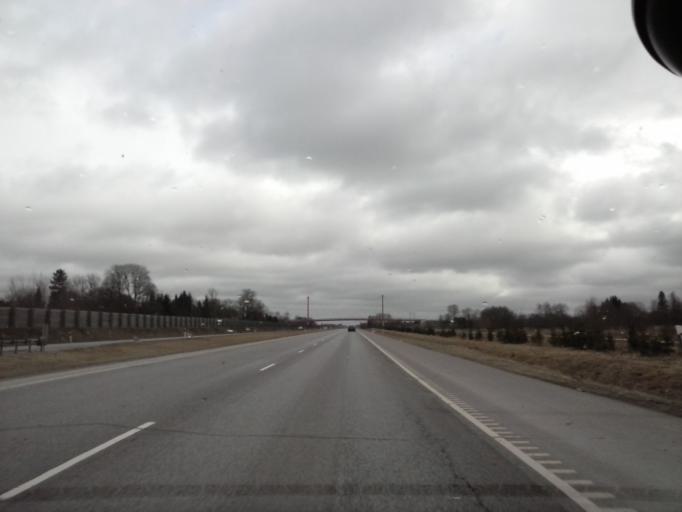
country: EE
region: Harju
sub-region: Rae vald
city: Vaida
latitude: 59.2846
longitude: 24.9734
